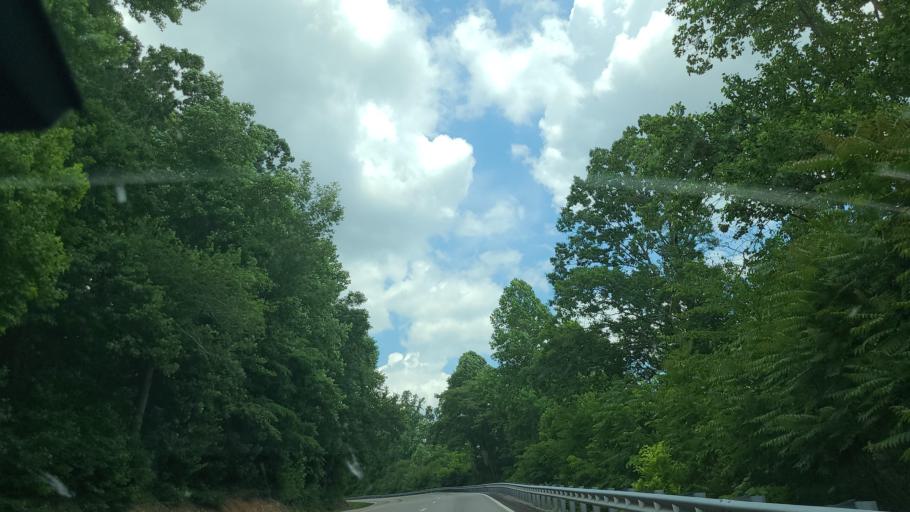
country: US
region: Tennessee
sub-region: Cumberland County
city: Lake Tansi
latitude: 35.7614
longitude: -85.0518
